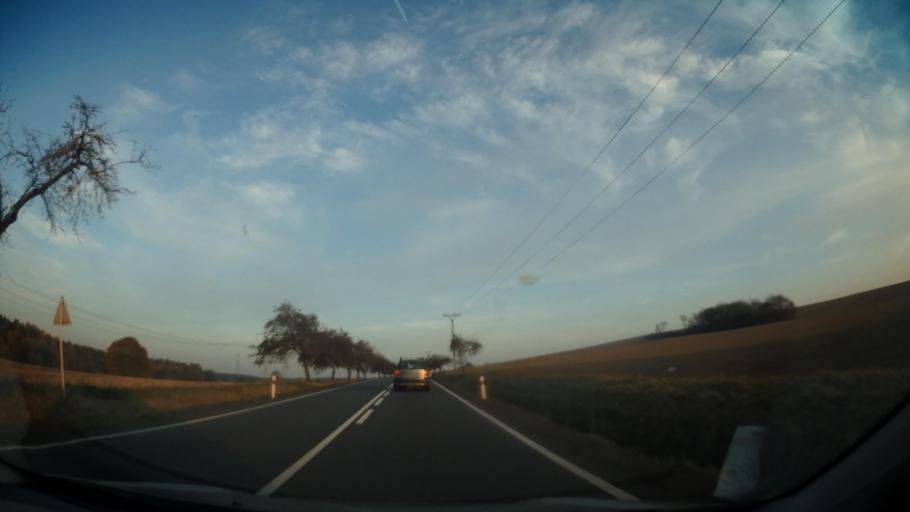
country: CZ
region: Central Bohemia
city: Trhovy Stepanov
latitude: 49.6628
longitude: 14.9869
